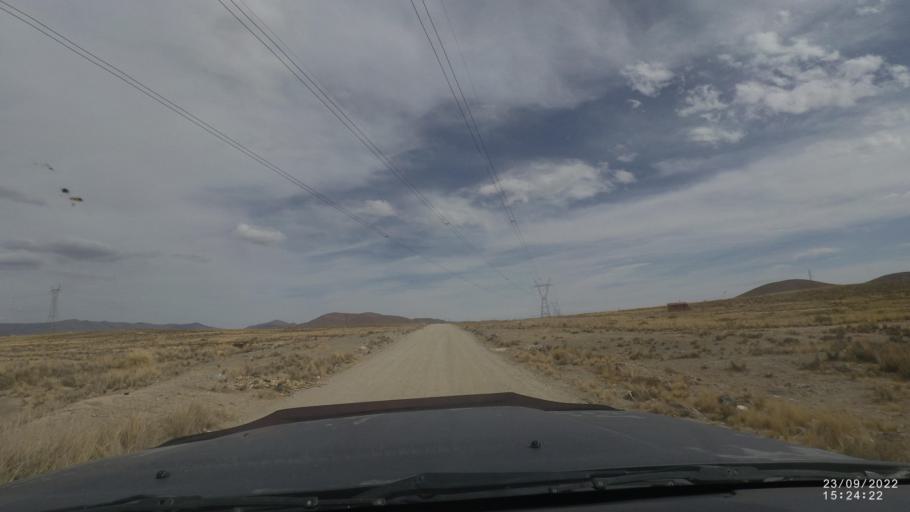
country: BO
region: Oruro
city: Oruro
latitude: -17.9344
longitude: -67.0407
